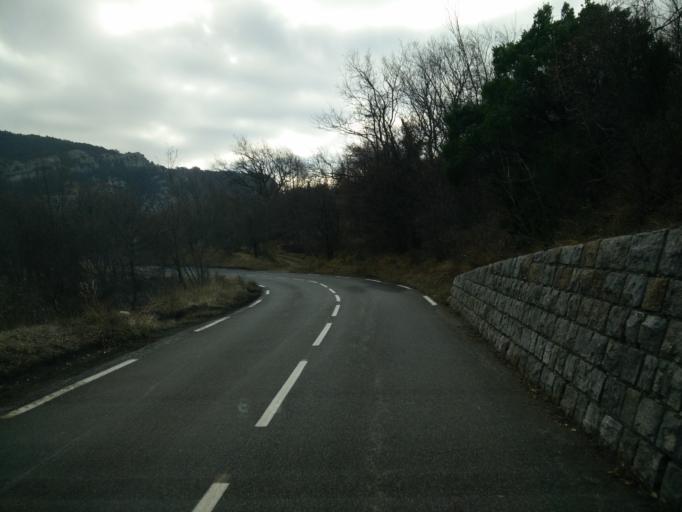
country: FR
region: Provence-Alpes-Cote d'Azur
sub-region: Departement des Alpes-Maritimes
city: Tourrettes-sur-Loup
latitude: 43.7374
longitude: 6.9942
